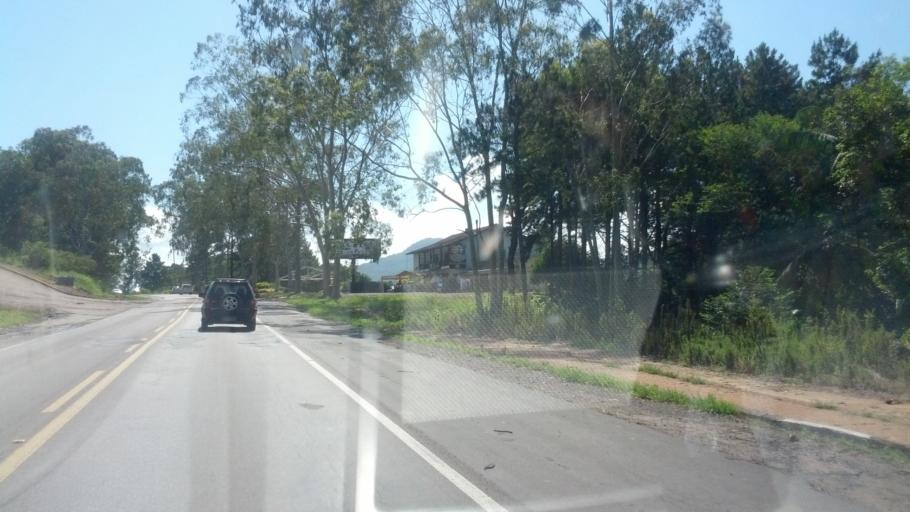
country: BR
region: Santa Catarina
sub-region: Rio Do Sul
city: Rio do Sul
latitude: -27.1884
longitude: -49.6117
